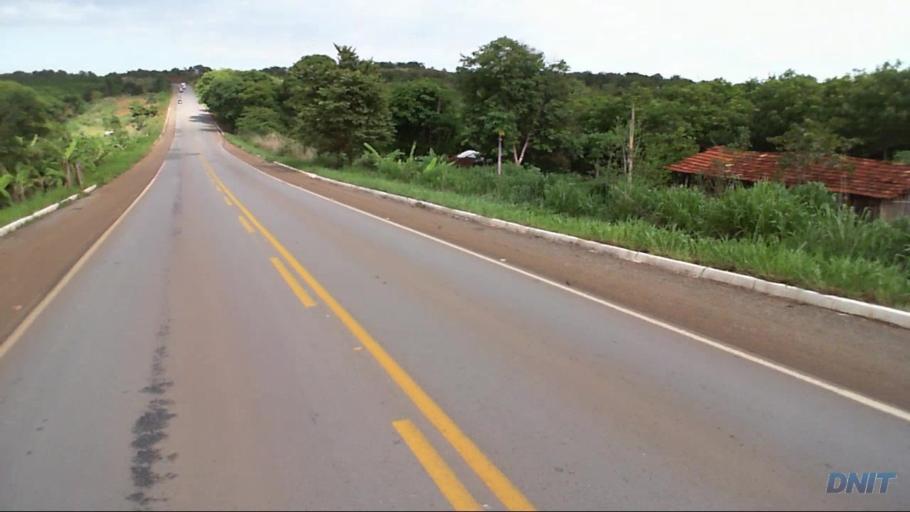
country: BR
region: Goias
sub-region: Barro Alto
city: Barro Alto
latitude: -14.8723
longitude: -49.0028
